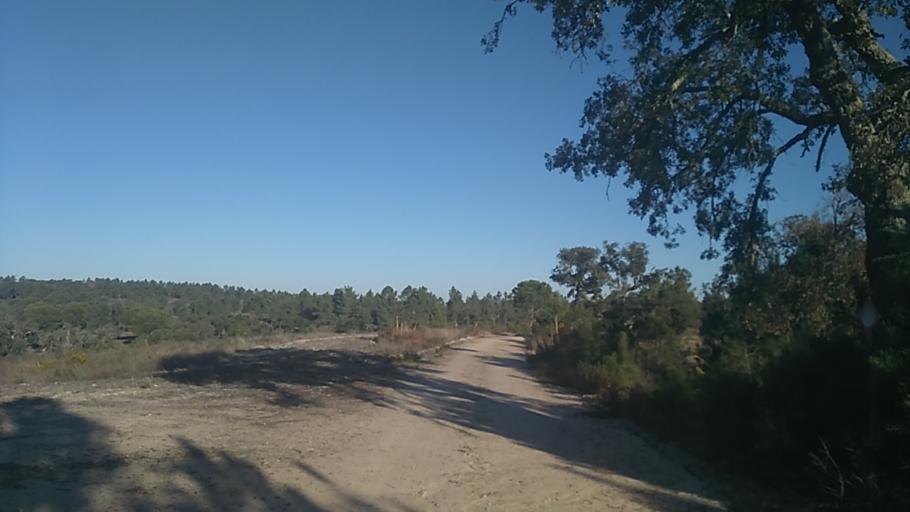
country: PT
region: Santarem
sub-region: Coruche
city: Coruche
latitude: 38.8653
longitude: -8.5244
